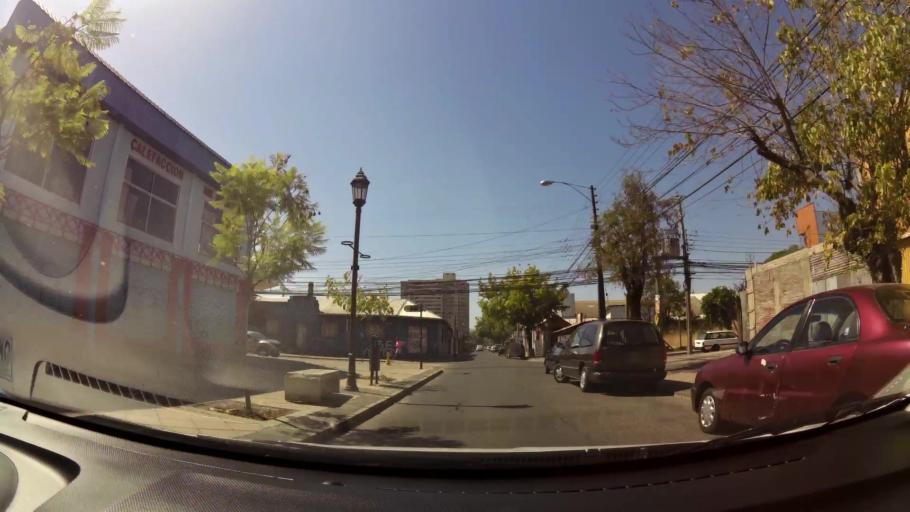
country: CL
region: Maule
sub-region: Provincia de Talca
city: Talca
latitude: -35.4315
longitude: -71.6587
